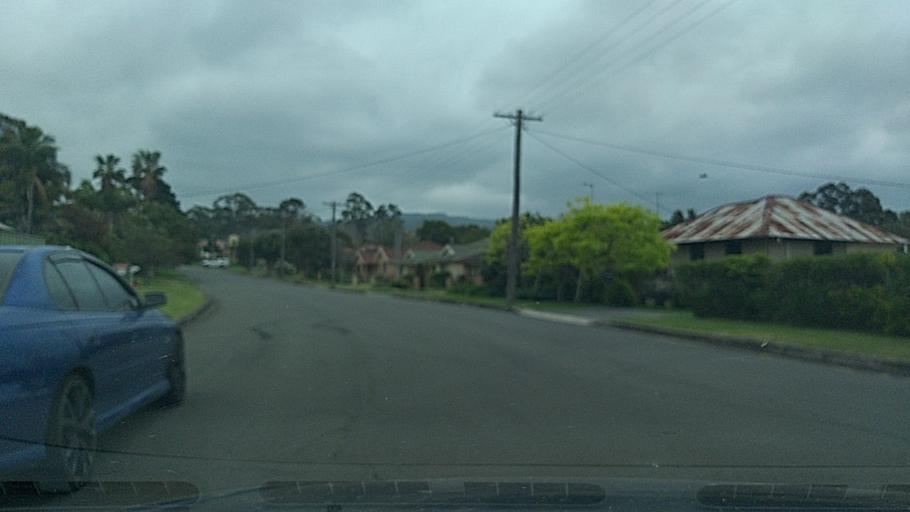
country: AU
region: New South Wales
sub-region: Wollongong
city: Cordeaux Heights
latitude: -34.4484
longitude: 150.8473
